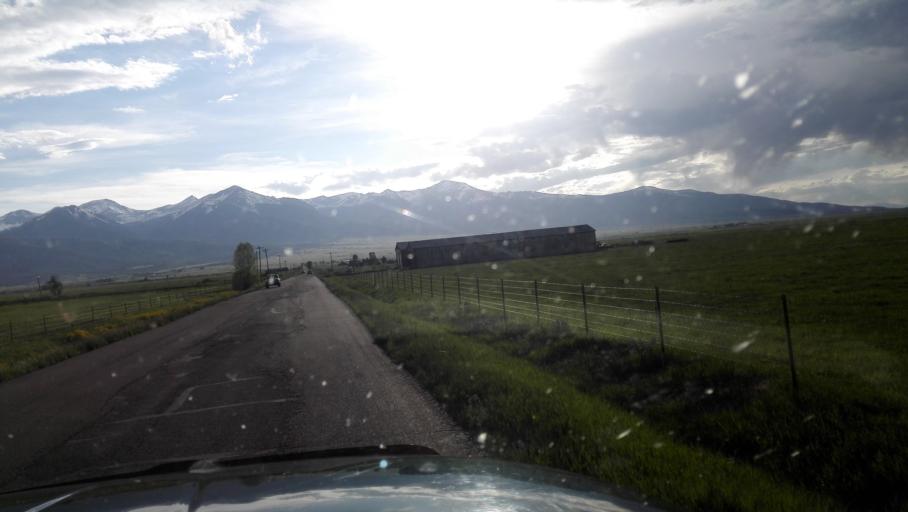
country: US
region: Colorado
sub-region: Custer County
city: Westcliffe
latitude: 38.1314
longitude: -105.4834
